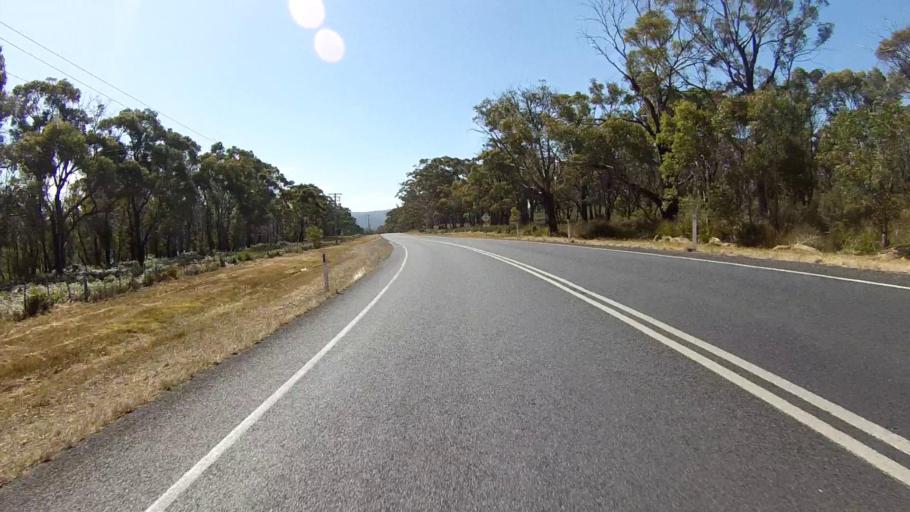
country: AU
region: Tasmania
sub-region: Sorell
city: Sorell
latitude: -42.5384
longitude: 147.8977
